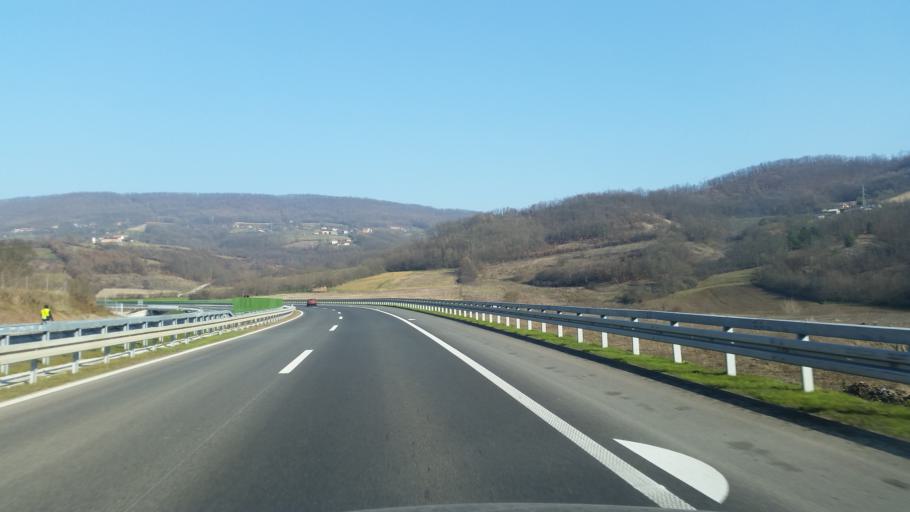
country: RS
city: Prislonica
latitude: 43.9941
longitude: 20.4015
